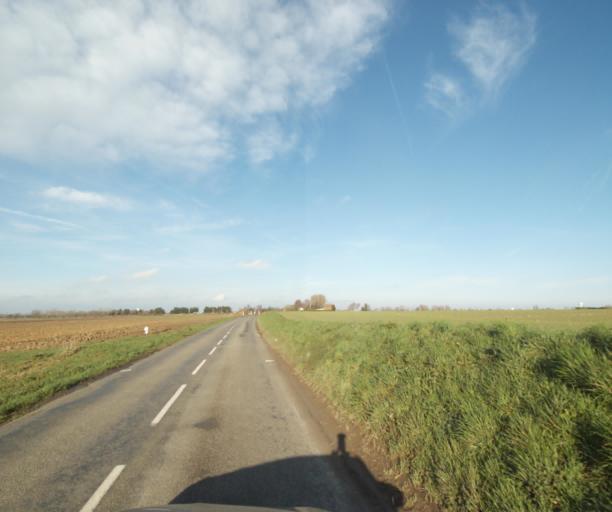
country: FR
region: Nord-Pas-de-Calais
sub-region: Departement du Nord
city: Saultain
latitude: 50.3253
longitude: 3.5746
